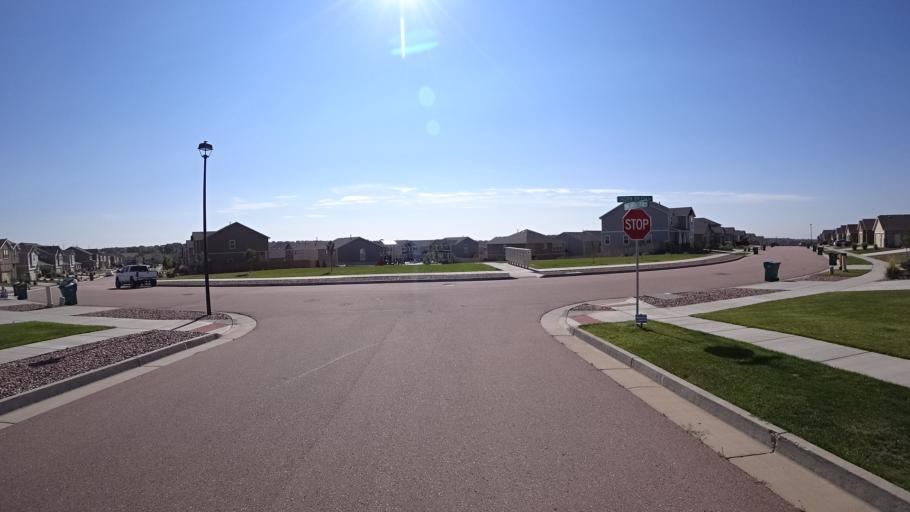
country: US
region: Colorado
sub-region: El Paso County
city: Cimarron Hills
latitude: 38.9349
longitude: -104.6962
